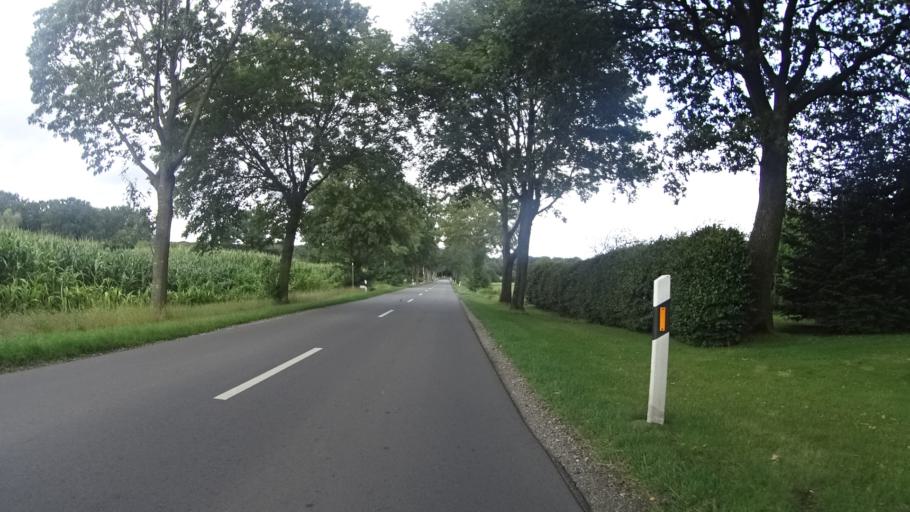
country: DE
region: Lower Saxony
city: Mittelstenahe
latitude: 53.6549
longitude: 9.0353
